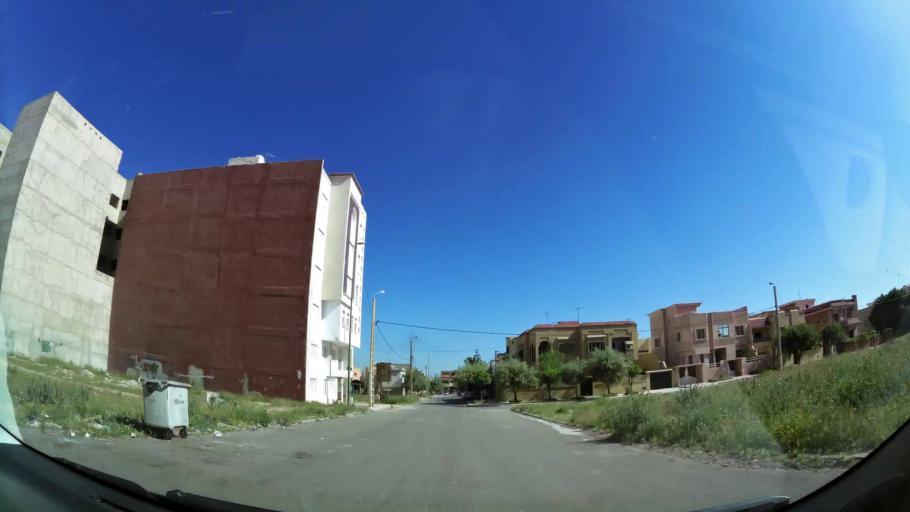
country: MA
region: Oriental
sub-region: Oujda-Angad
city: Oujda
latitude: 34.6617
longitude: -1.8981
